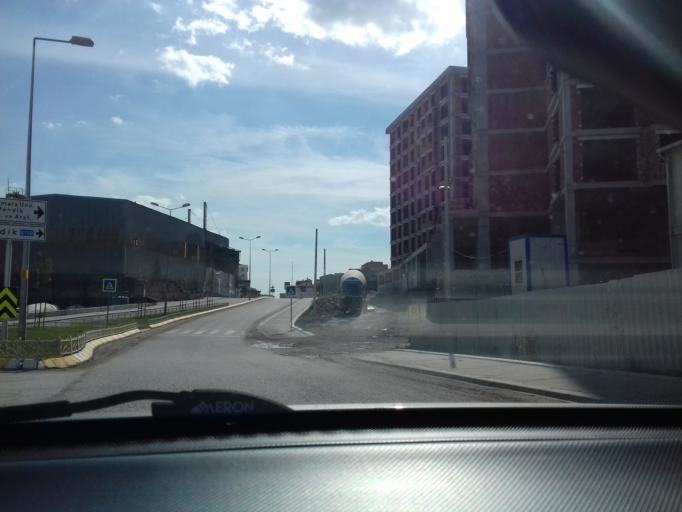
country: TR
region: Istanbul
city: Pendik
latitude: 40.8977
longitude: 29.2798
